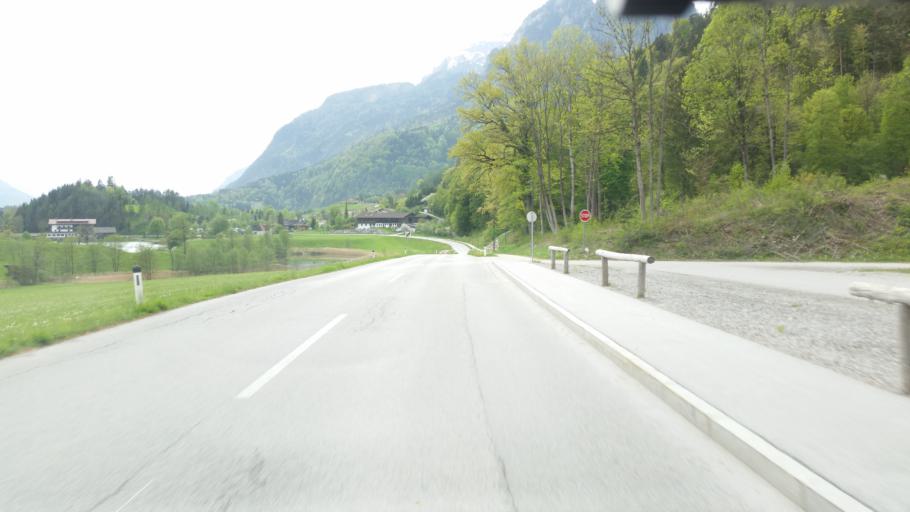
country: AT
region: Tyrol
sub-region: Politischer Bezirk Kufstein
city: Kramsach
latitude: 47.4596
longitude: 11.8880
